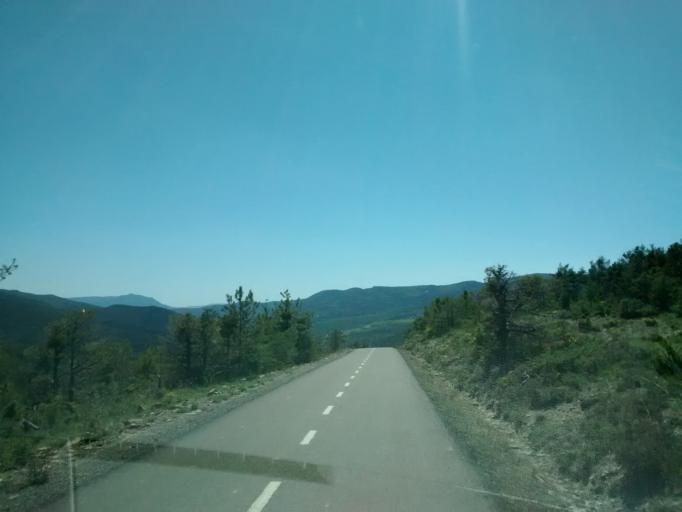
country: ES
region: Aragon
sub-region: Provincia de Huesca
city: Borau
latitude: 42.6741
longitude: -0.6136
